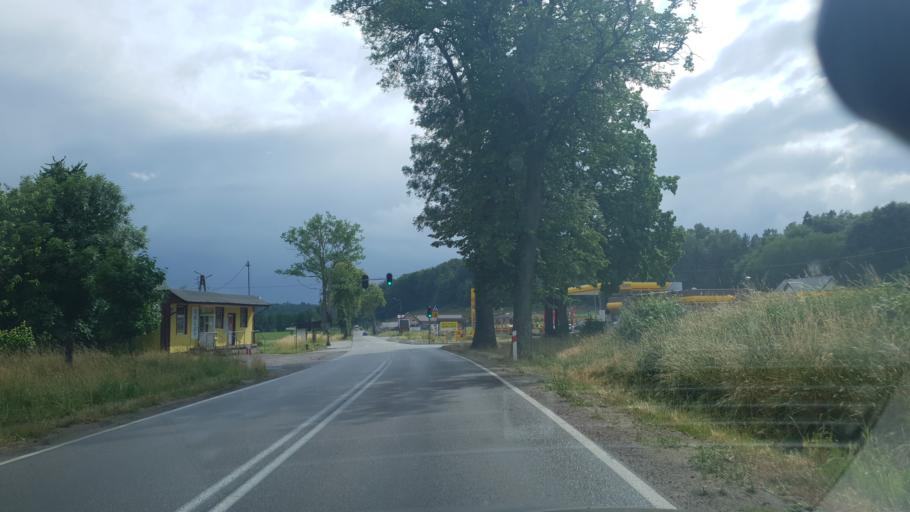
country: PL
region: Pomeranian Voivodeship
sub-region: Powiat kartuski
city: Chmielno
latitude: 54.3052
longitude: 18.1480
